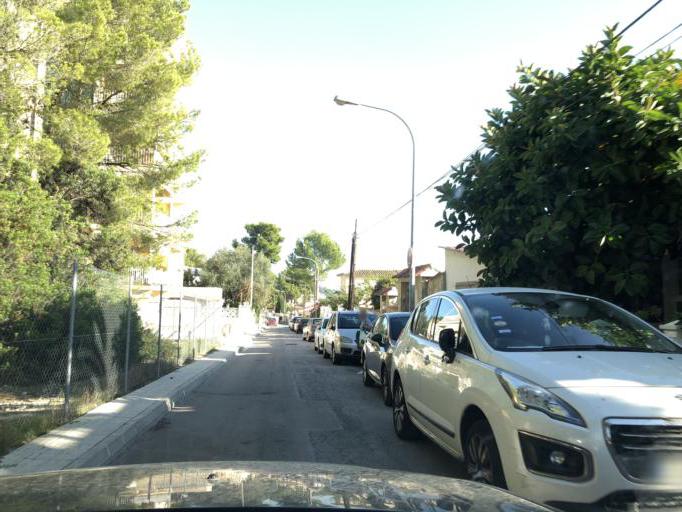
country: ES
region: Balearic Islands
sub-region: Illes Balears
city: Camp de Mar
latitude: 39.5399
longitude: 2.4404
